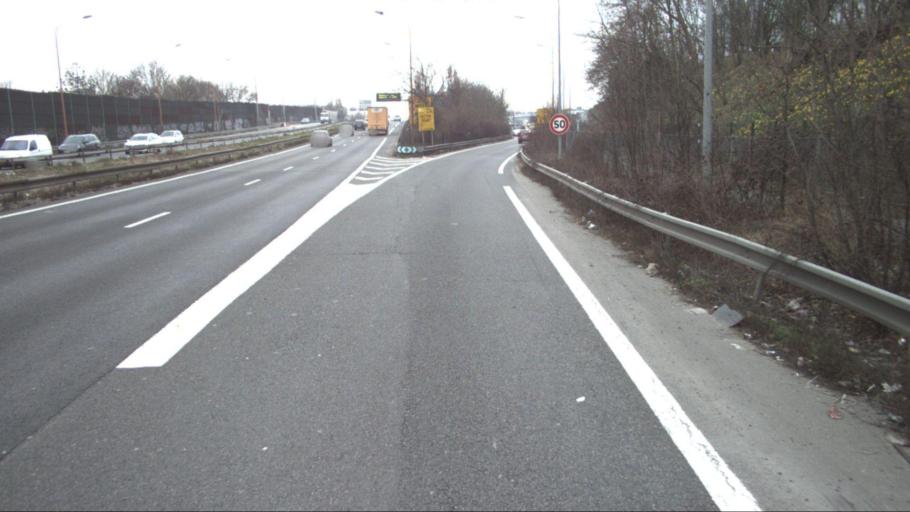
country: FR
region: Ile-de-France
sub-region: Departement du Val-d'Oise
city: Bezons
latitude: 48.9211
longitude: 2.2254
